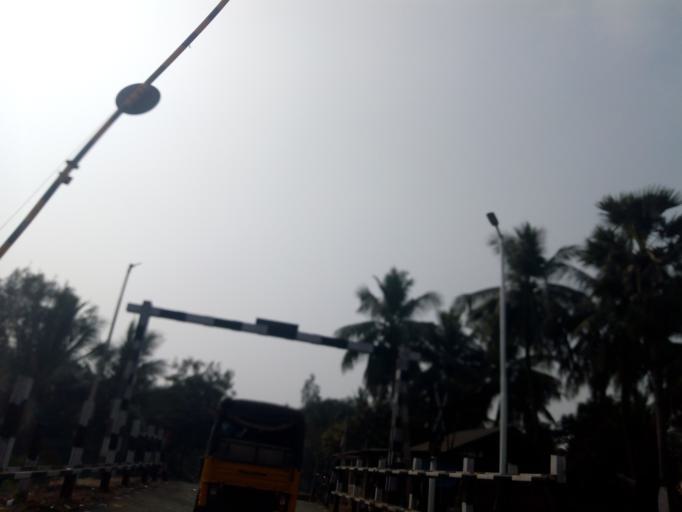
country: IN
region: Andhra Pradesh
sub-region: West Godavari
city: Tadepallegudem
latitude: 16.8152
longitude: 81.3632
